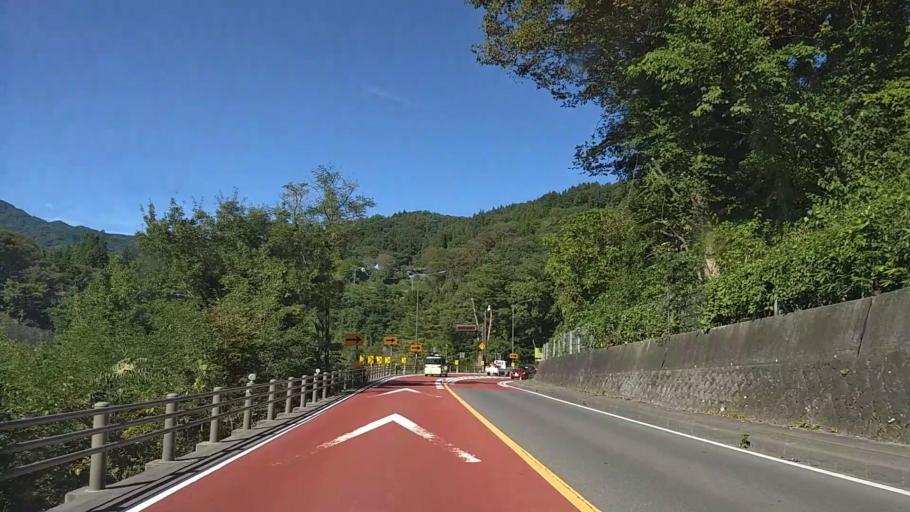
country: JP
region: Nagano
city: Nagano-shi
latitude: 36.6206
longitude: 138.1046
